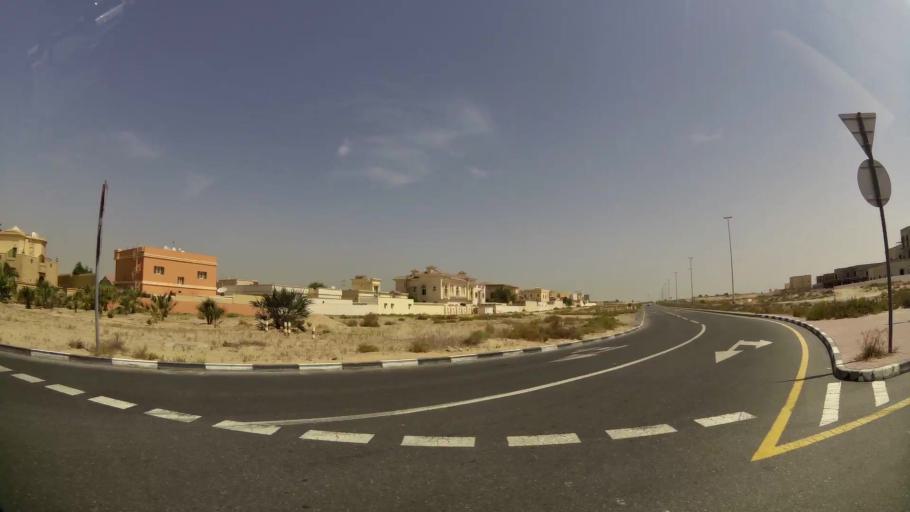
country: AE
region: Ash Shariqah
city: Sharjah
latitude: 25.1845
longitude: 55.4275
